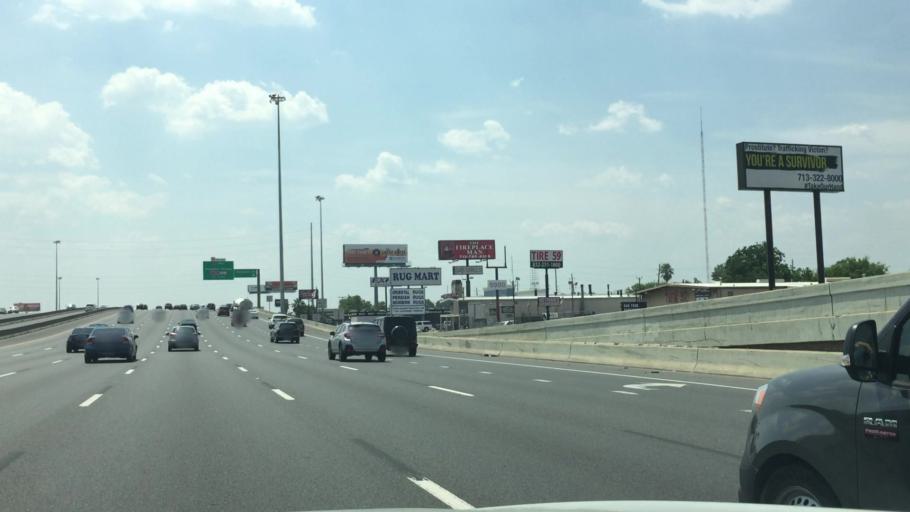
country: US
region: Texas
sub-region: Harris County
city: Bellaire
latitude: 29.7261
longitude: -95.4809
